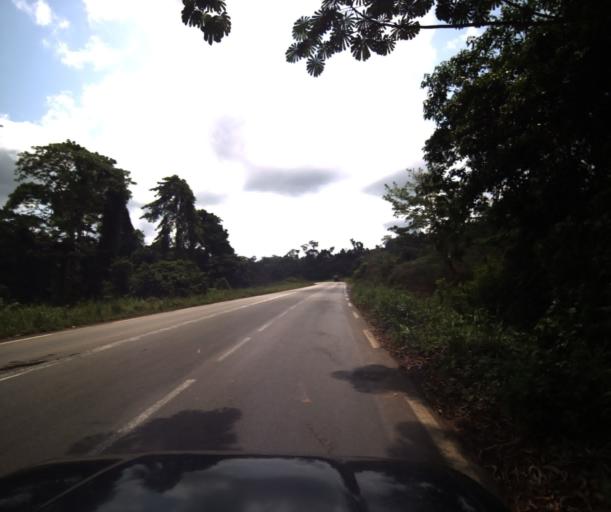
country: CM
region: Centre
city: Eseka
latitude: 3.8732
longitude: 10.8275
